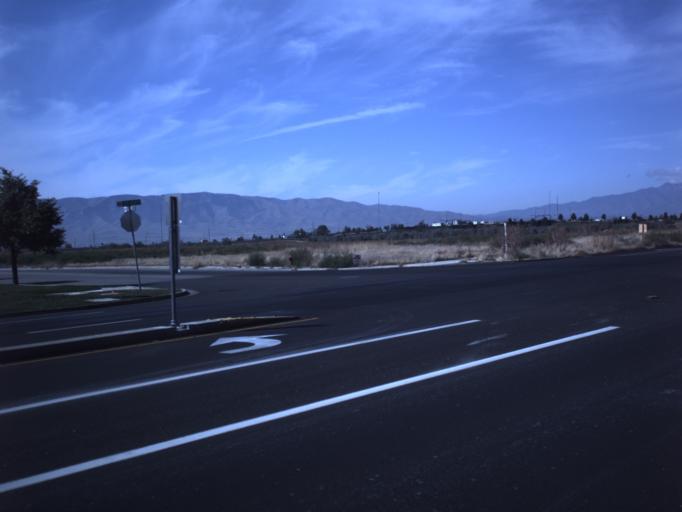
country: US
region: Utah
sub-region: Utah County
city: Pleasant Grove
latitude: 40.3510
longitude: -111.7585
